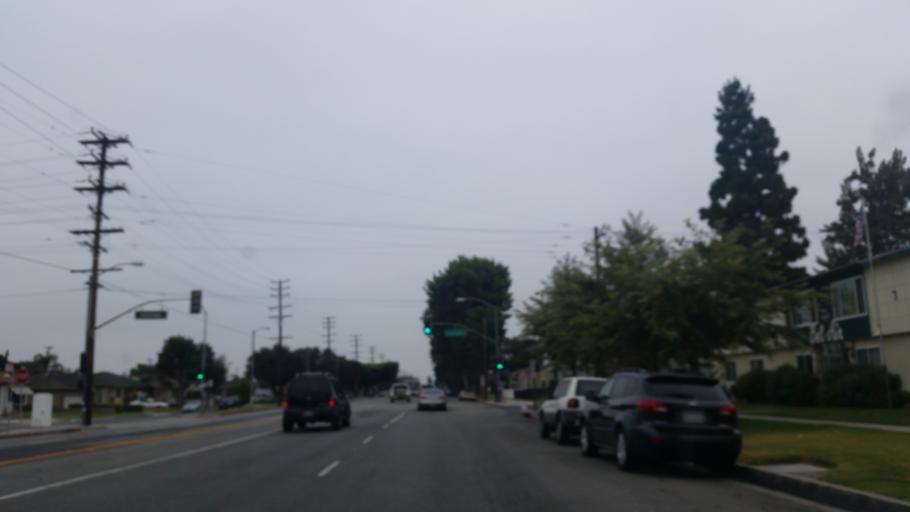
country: US
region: California
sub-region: Los Angeles County
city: Lakewood
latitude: 33.8401
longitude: -118.1252
